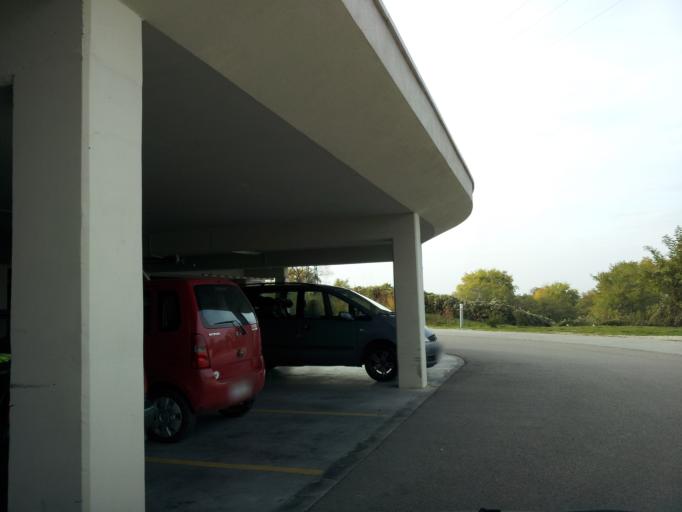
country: HU
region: Gyor-Moson-Sopron
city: Pannonhalma
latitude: 47.5553
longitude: 17.7602
